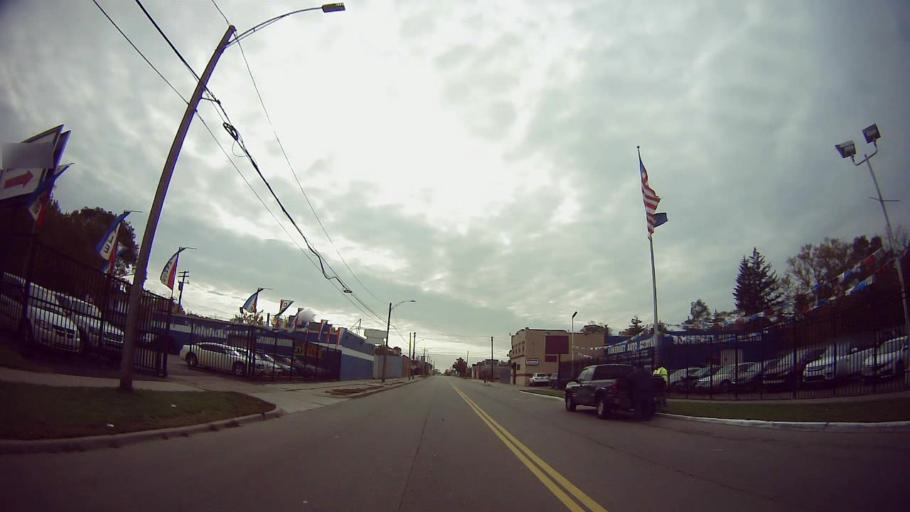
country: US
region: Michigan
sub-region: Oakland County
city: Hazel Park
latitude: 42.4453
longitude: -83.1028
